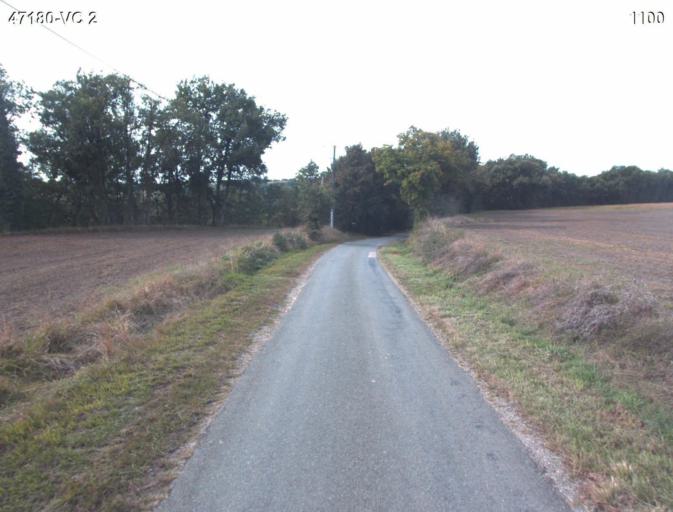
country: FR
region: Aquitaine
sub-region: Departement du Lot-et-Garonne
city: Sainte-Colombe-en-Bruilhois
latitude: 44.1658
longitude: 0.4333
